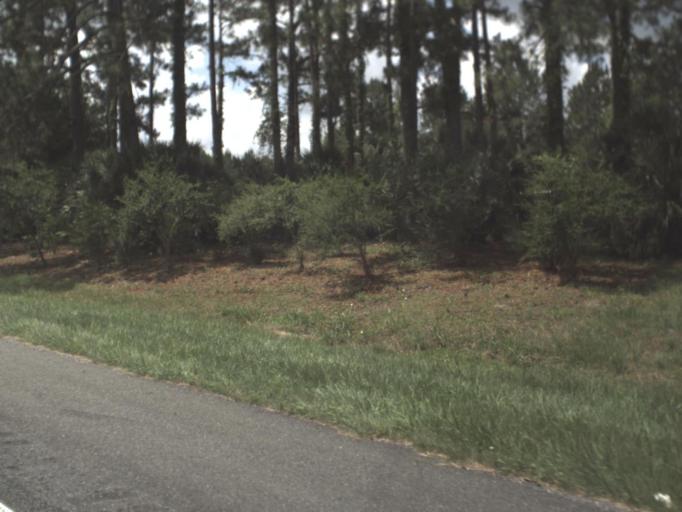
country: US
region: Florida
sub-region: Suwannee County
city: Wellborn
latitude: 30.2666
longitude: -82.7545
